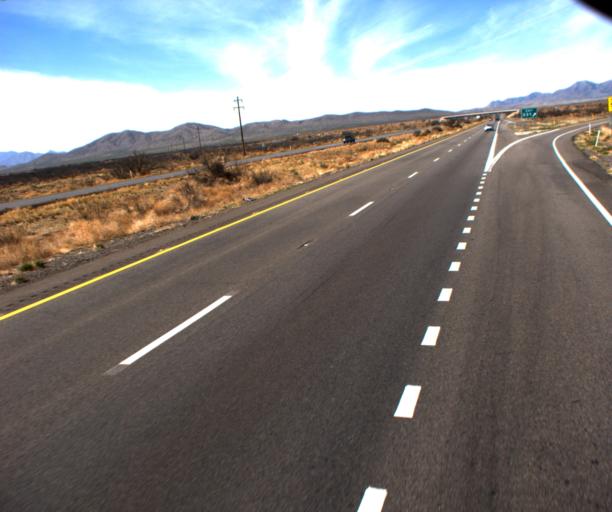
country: US
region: Arizona
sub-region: Cochise County
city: Willcox
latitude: 32.1800
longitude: -109.9439
